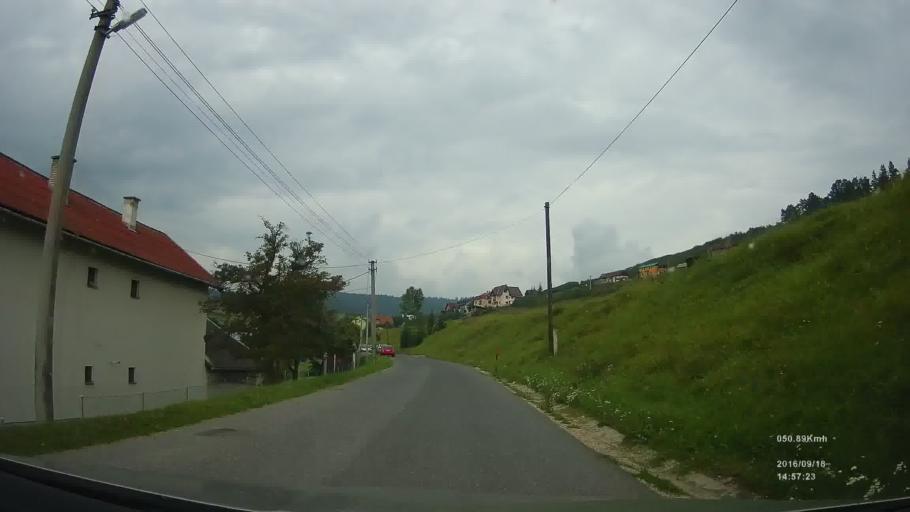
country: SK
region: Presovsky
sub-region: Okres Presov
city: Levoca
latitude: 49.0217
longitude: 20.5247
